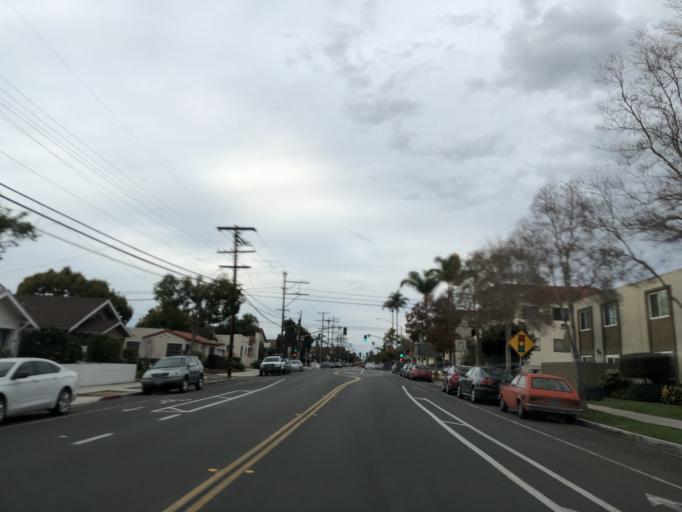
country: US
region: California
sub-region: San Diego County
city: San Diego
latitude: 32.7454
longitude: -117.1513
